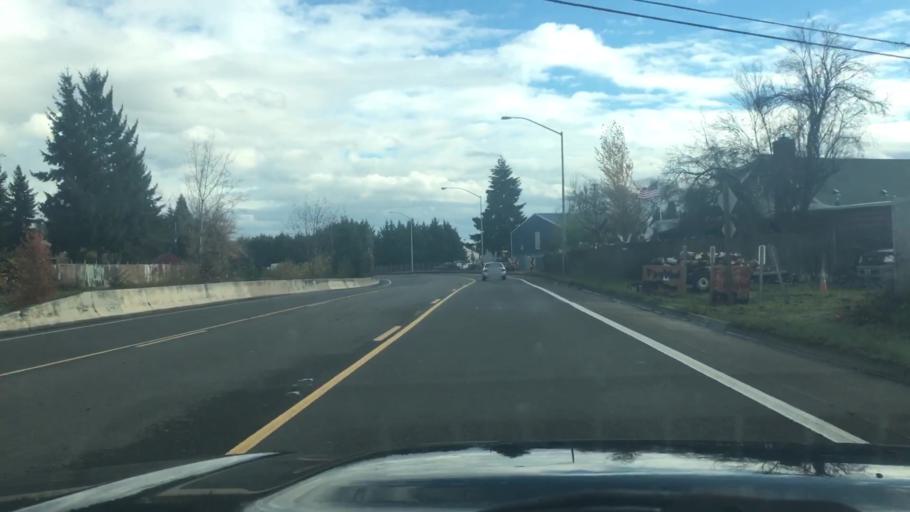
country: US
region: Oregon
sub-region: Lane County
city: Eugene
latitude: 44.0638
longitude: -123.1589
